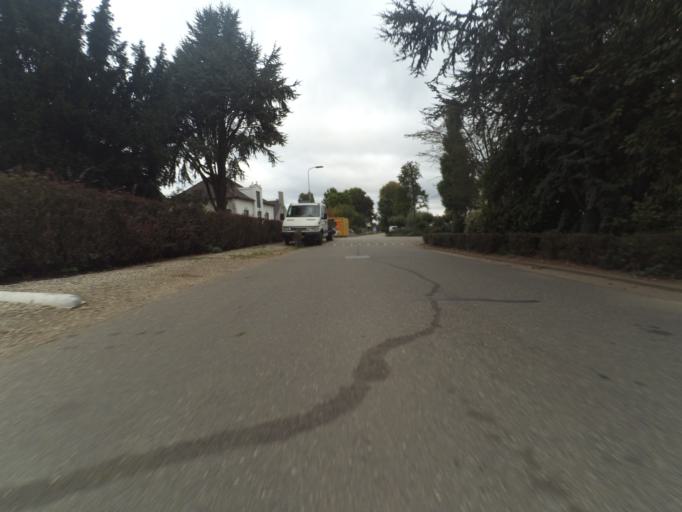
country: NL
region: Gelderland
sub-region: Gemeente Buren
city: Lienden
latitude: 51.9530
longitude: 5.5150
